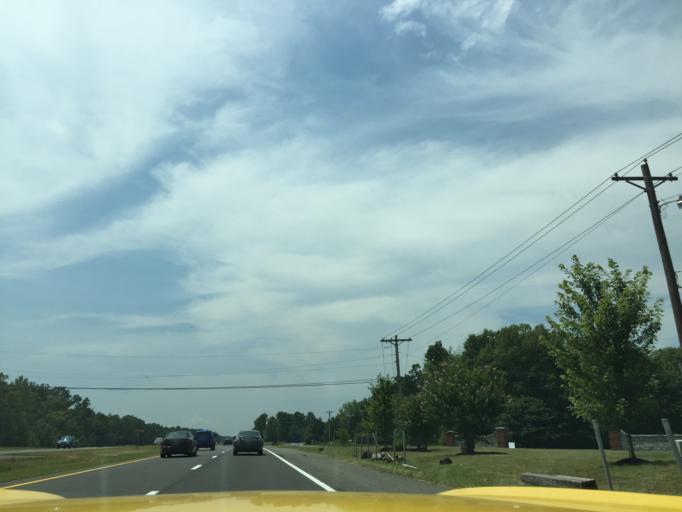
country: US
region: Maryland
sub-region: Prince George's County
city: Accokeek
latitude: 38.6570
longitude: -77.0274
